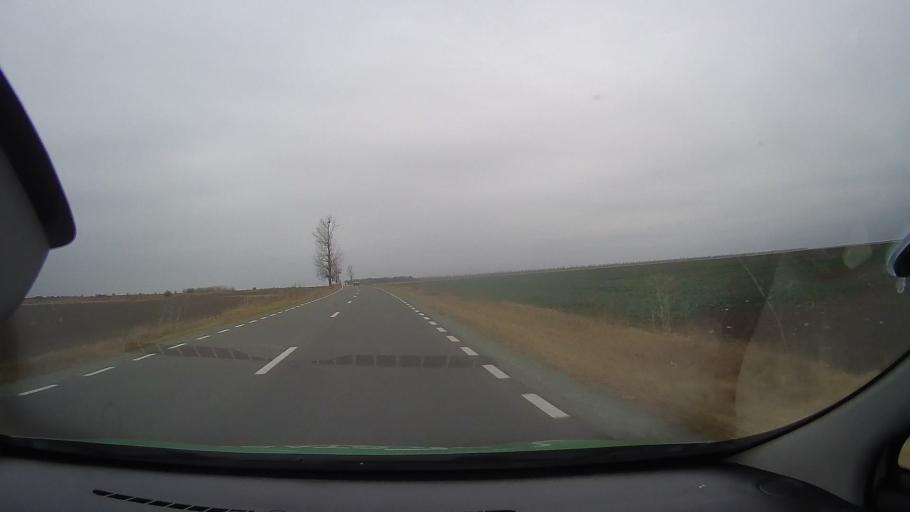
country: RO
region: Ialomita
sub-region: Comuna Scanteia
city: Iazu
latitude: 44.7144
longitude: 27.4193
